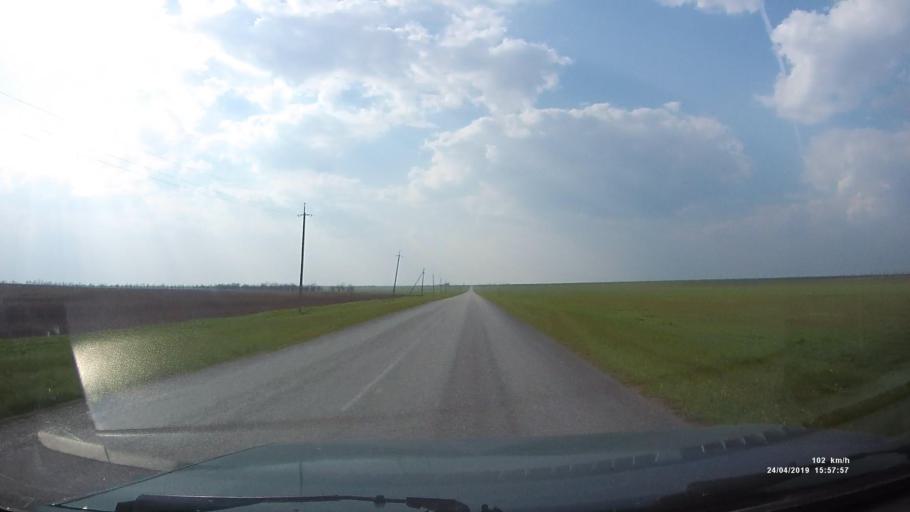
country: RU
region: Kalmykiya
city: Yashalta
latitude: 46.6097
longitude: 42.4990
